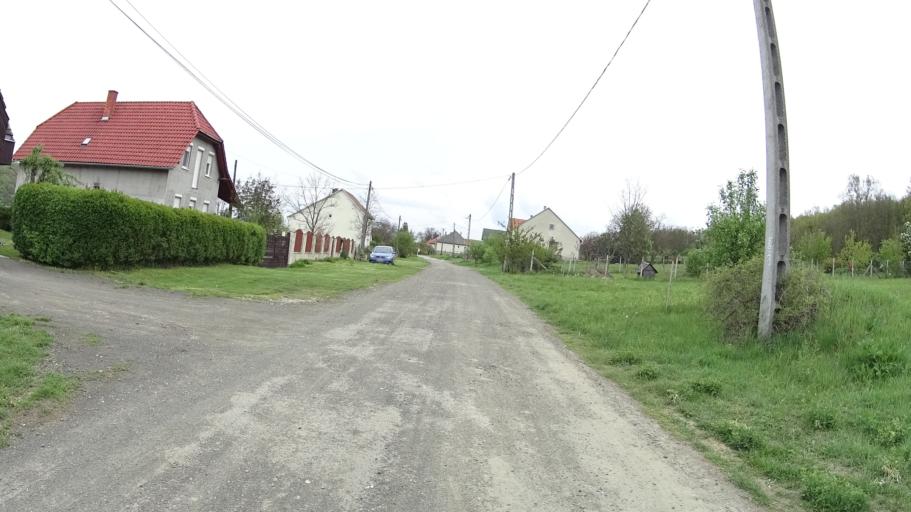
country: HU
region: Pest
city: Acsa
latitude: 47.8148
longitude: 19.3156
